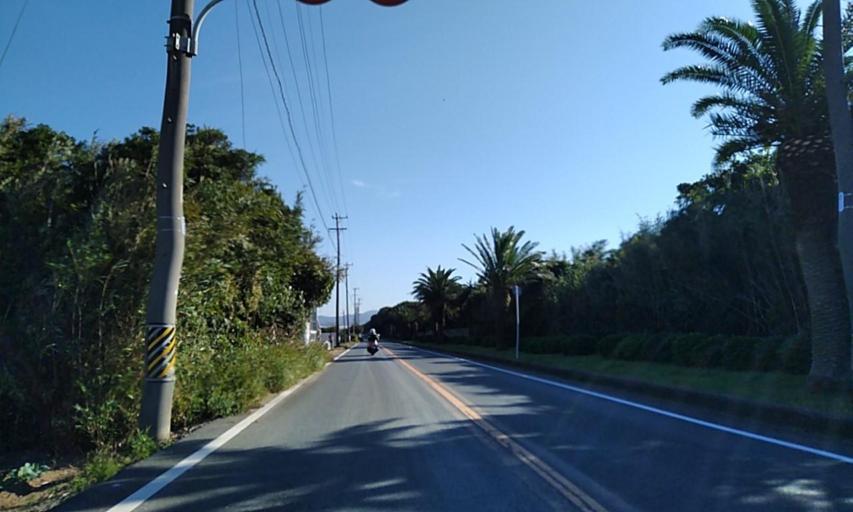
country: JP
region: Aichi
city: Toyohama
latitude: 34.5859
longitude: 137.0626
